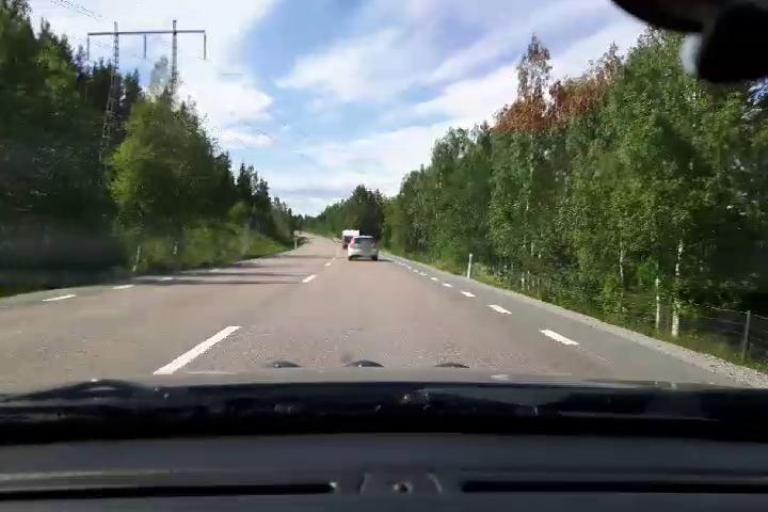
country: SE
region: Gaevleborg
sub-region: Bollnas Kommun
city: Kilafors
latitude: 61.2837
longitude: 16.5177
